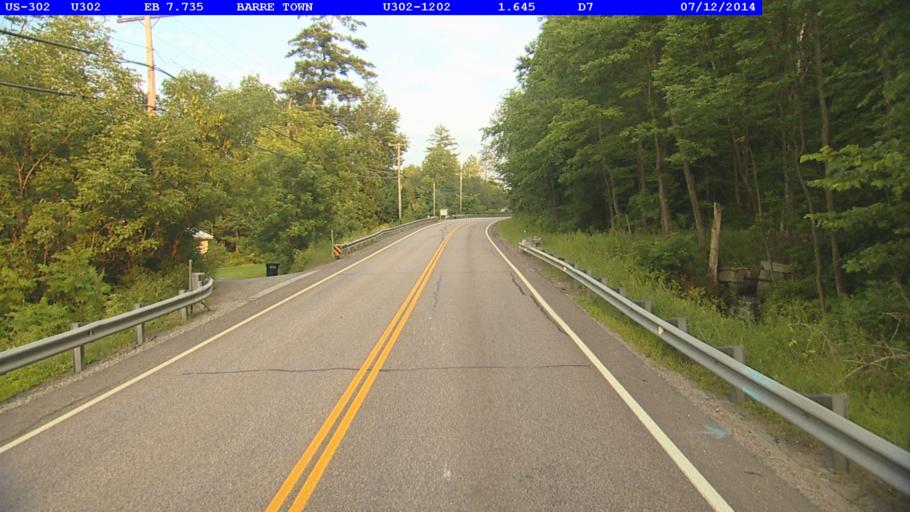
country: US
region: Vermont
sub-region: Washington County
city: South Barre
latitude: 44.1694
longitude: -72.4615
